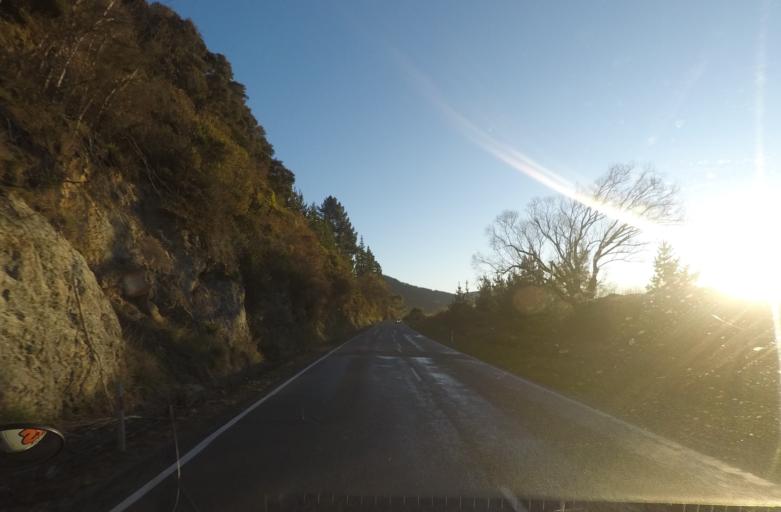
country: NZ
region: Marlborough
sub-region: Marlborough District
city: Picton
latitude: -41.2876
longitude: 173.6848
